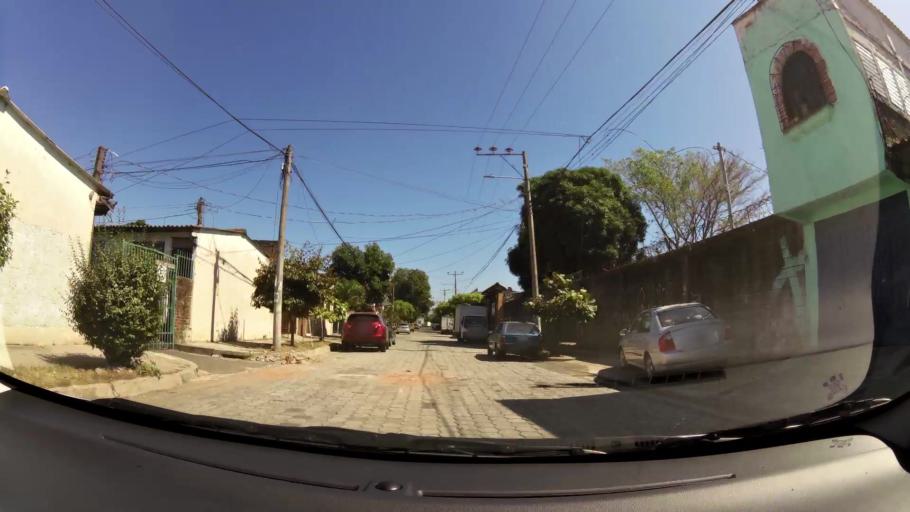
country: SV
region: La Libertad
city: Santa Tecla
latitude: 13.6746
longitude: -89.2956
